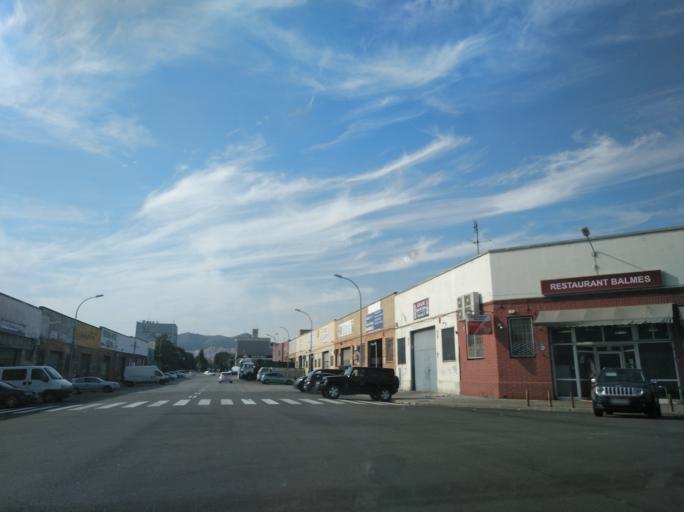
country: ES
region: Catalonia
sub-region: Provincia de Barcelona
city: Sant Adria de Besos
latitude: 41.4314
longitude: 2.2078
